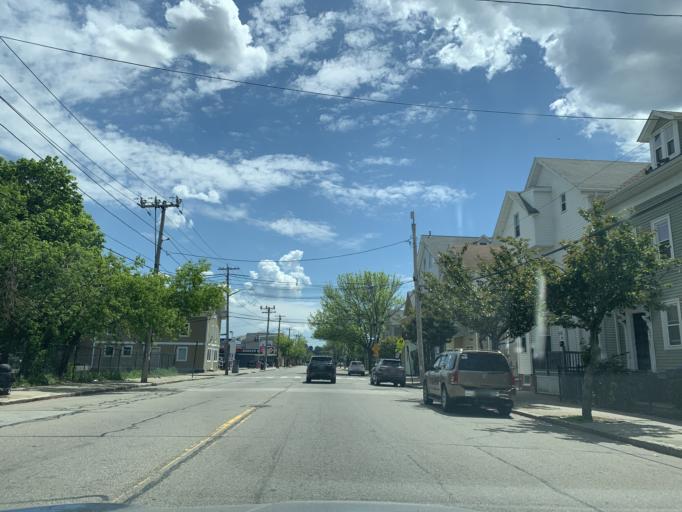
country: US
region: Rhode Island
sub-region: Providence County
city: Providence
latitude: 41.8374
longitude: -71.4230
